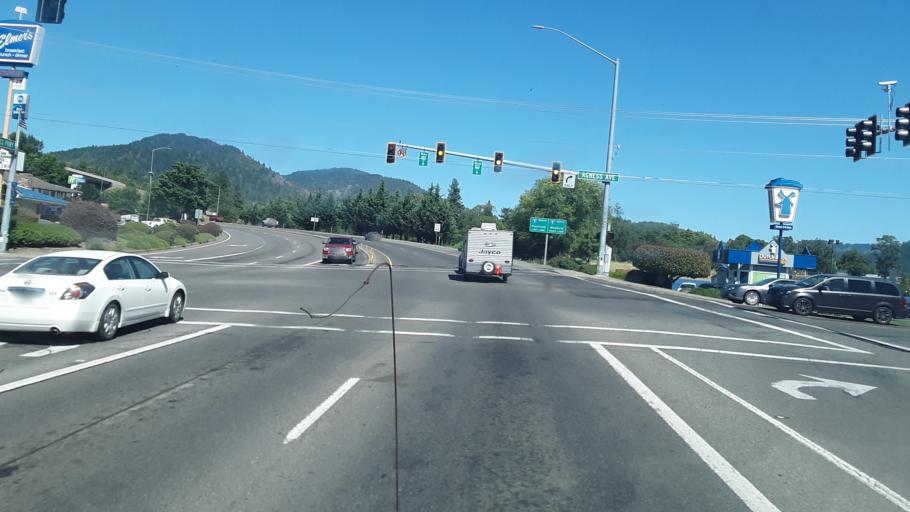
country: US
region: Oregon
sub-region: Josephine County
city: Fruitdale
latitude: 42.4364
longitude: -123.2986
